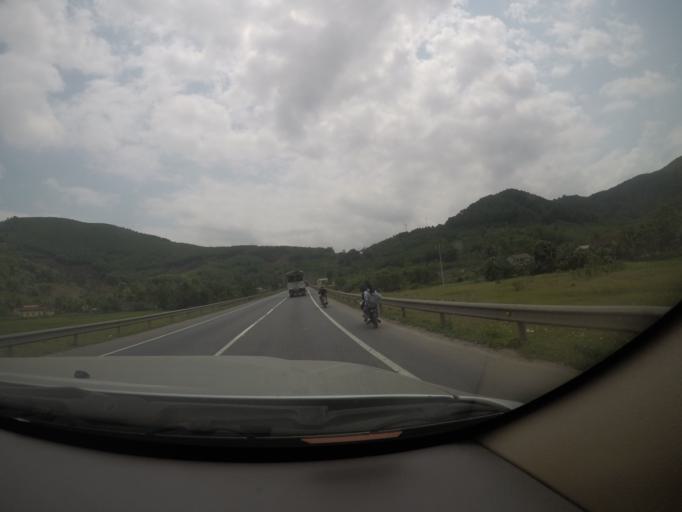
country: VN
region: Thua Thien-Hue
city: Phu Loc
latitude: 16.2815
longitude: 107.9107
